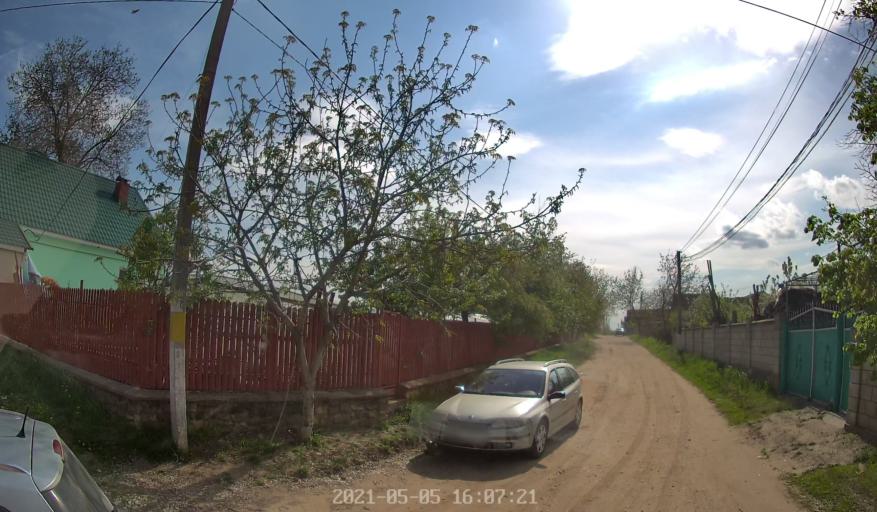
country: MD
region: Criuleni
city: Criuleni
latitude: 47.1427
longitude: 29.2006
